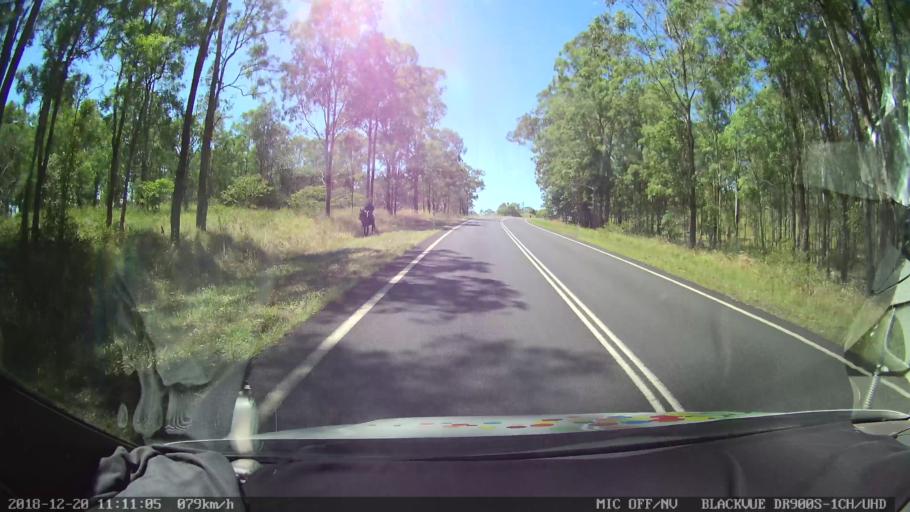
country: AU
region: New South Wales
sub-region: Richmond Valley
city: Casino
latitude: -28.9572
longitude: 153.0126
